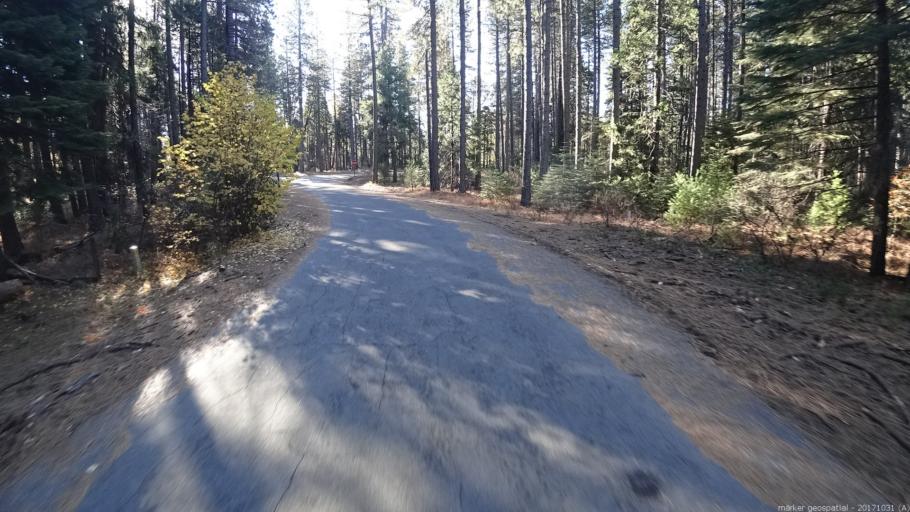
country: US
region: California
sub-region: Shasta County
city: Shingletown
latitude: 40.5085
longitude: -121.8253
